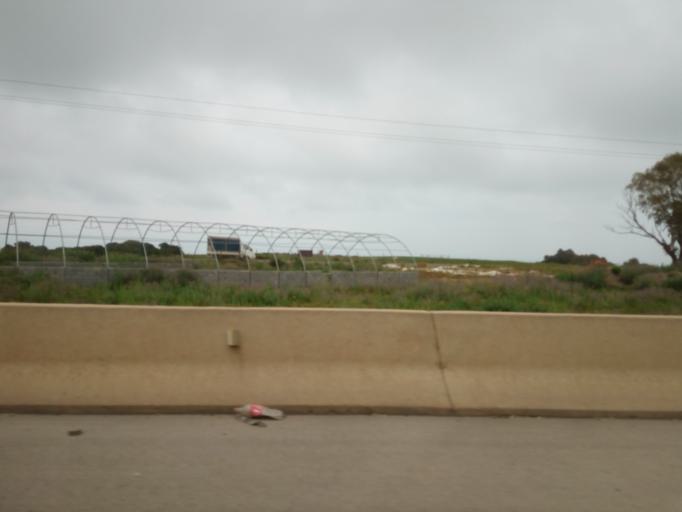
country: DZ
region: Tipaza
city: Bou Ismail
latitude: 36.5982
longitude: 2.6397
